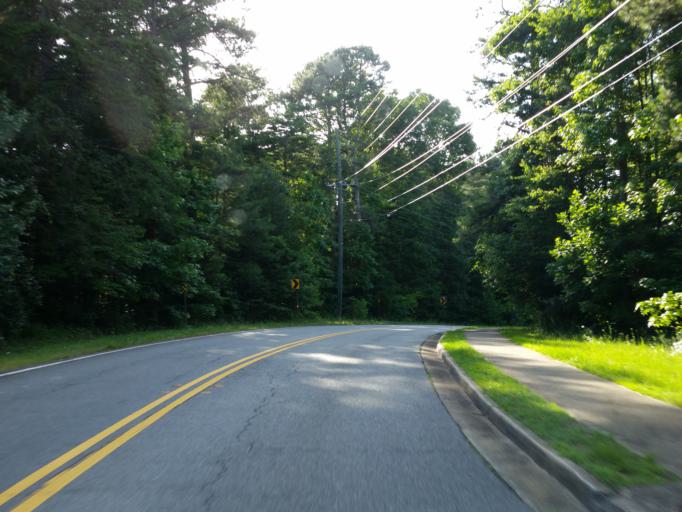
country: US
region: Georgia
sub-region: Cherokee County
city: Woodstock
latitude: 34.0629
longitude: -84.4834
